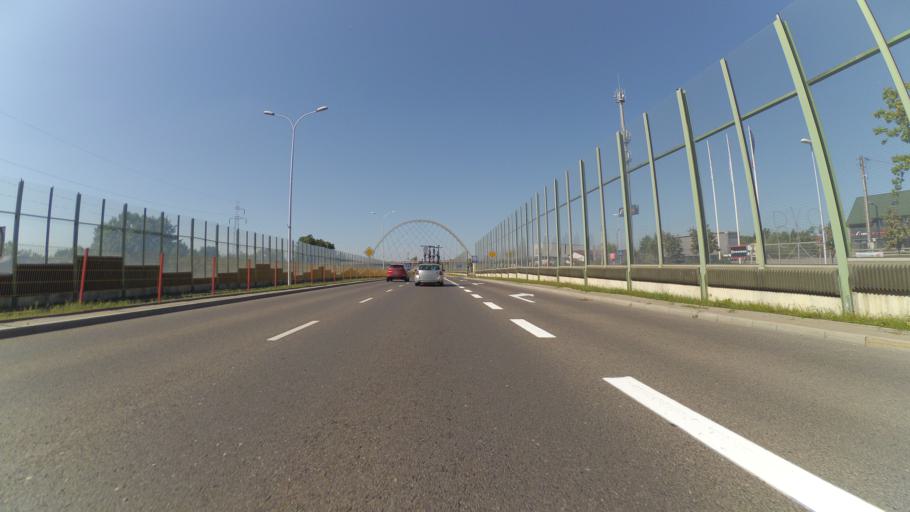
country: PL
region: Podlasie
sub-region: Bialystok
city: Bialystok
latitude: 53.1595
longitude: 23.1262
